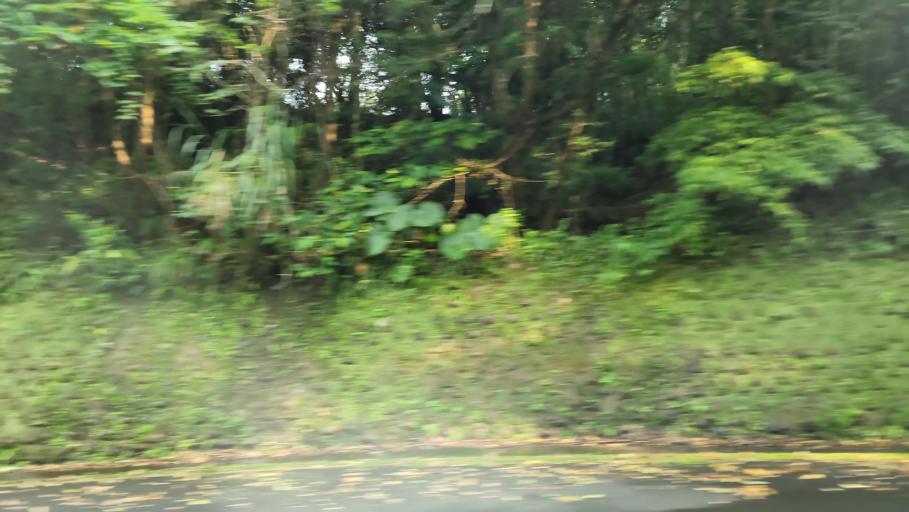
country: TW
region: Taiwan
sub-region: Keelung
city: Keelung
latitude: 25.1550
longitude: 121.6429
